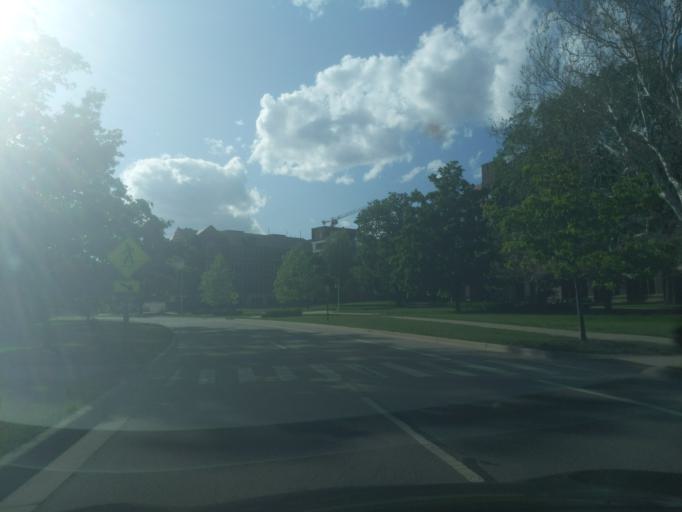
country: US
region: Michigan
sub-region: Ingham County
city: East Lansing
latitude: 42.7331
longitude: -84.4814
